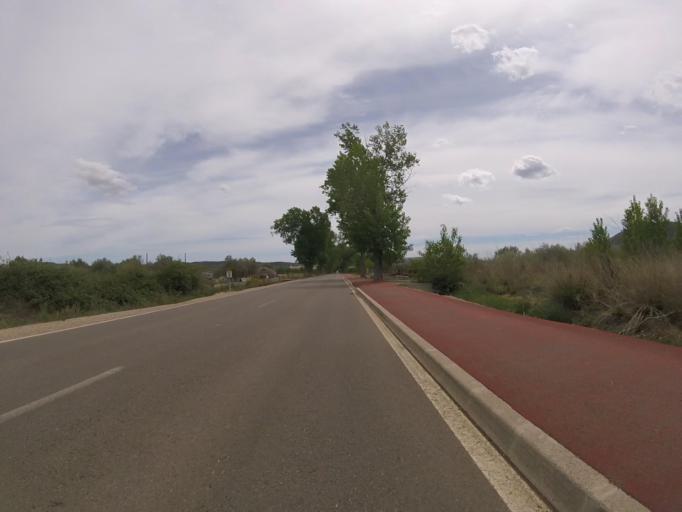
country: ES
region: Valencia
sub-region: Provincia de Castello
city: Cabanes
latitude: 40.1639
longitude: 0.0194
